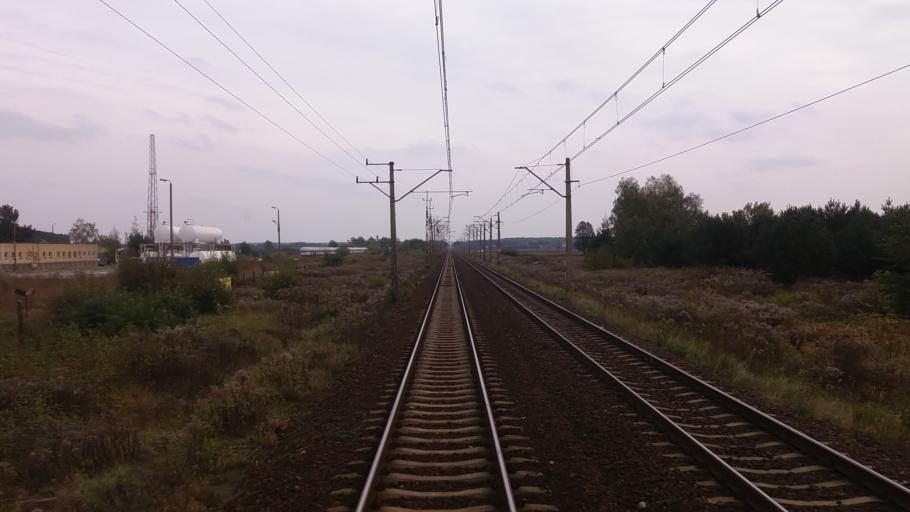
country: PL
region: West Pomeranian Voivodeship
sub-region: Powiat gryfinski
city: Stare Czarnowo
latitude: 53.3879
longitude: 14.7203
